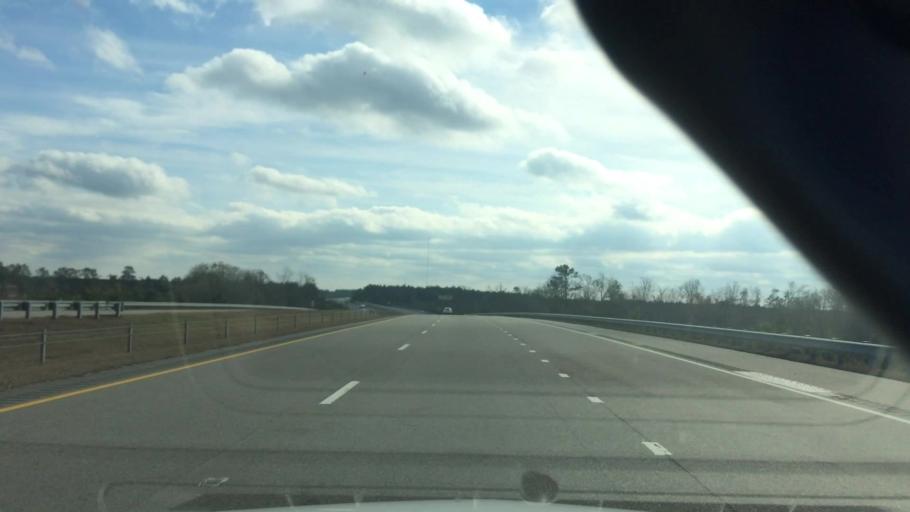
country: US
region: North Carolina
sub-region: Brunswick County
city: Leland
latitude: 34.2570
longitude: -78.0799
